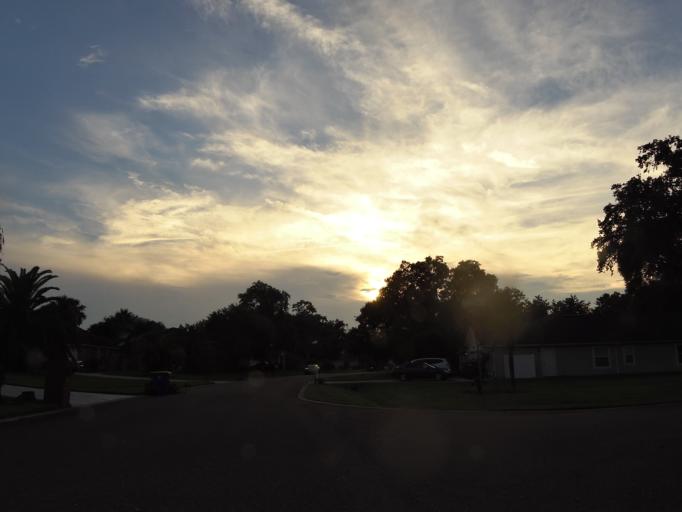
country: US
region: Florida
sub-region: Duval County
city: Atlantic Beach
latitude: 30.3953
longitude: -81.4996
